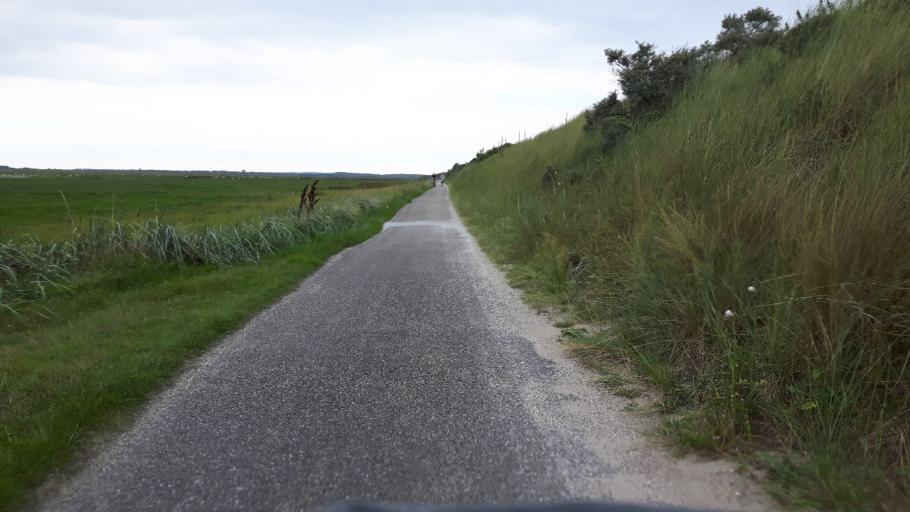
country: NL
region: Friesland
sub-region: Gemeente Ameland
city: Nes
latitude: 53.4607
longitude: 5.8685
